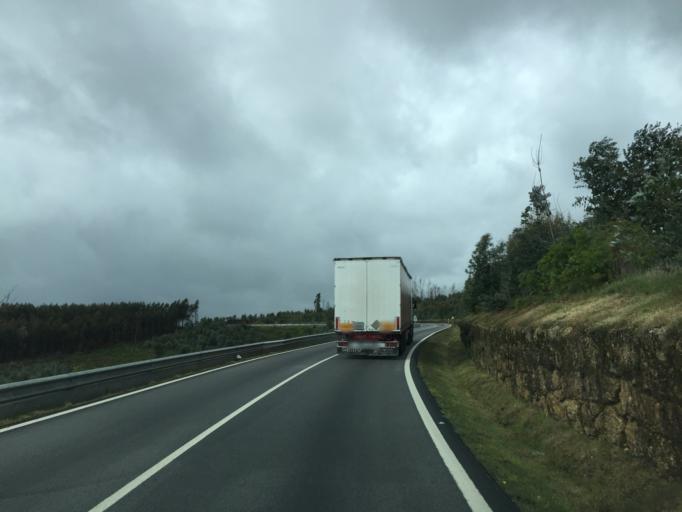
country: PT
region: Coimbra
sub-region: Oliveira do Hospital
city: Oliveira do Hospital
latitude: 40.3229
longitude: -7.9275
